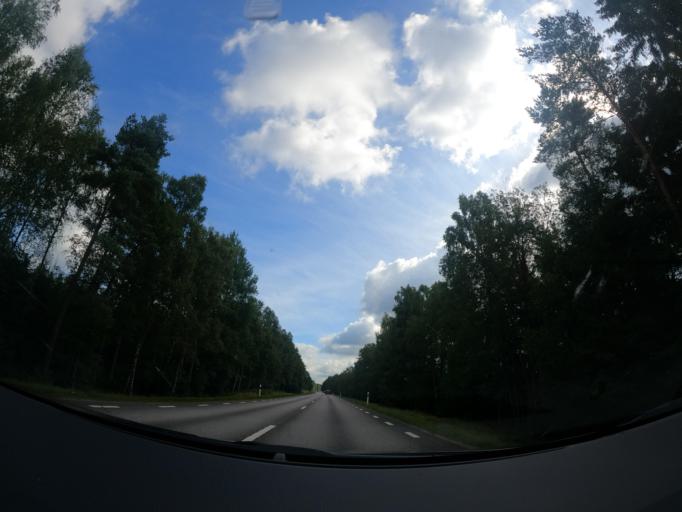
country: SE
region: Halland
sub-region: Hylte Kommun
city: Torup
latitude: 57.1276
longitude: 13.1229
